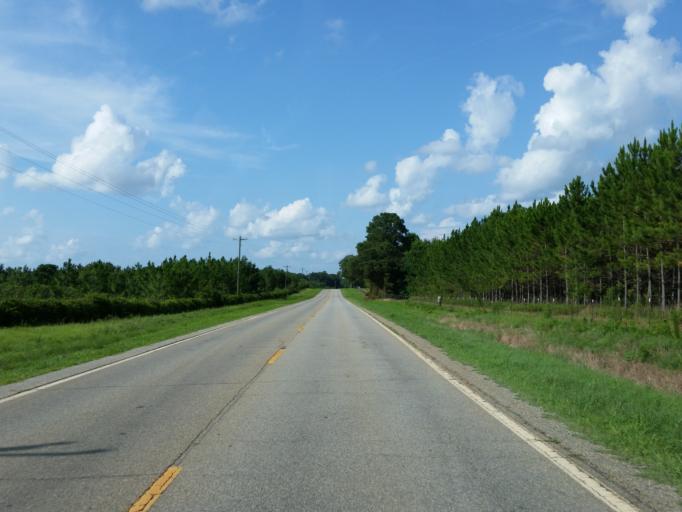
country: US
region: Georgia
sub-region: Lee County
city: Leesburg
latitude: 31.8065
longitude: -84.1184
